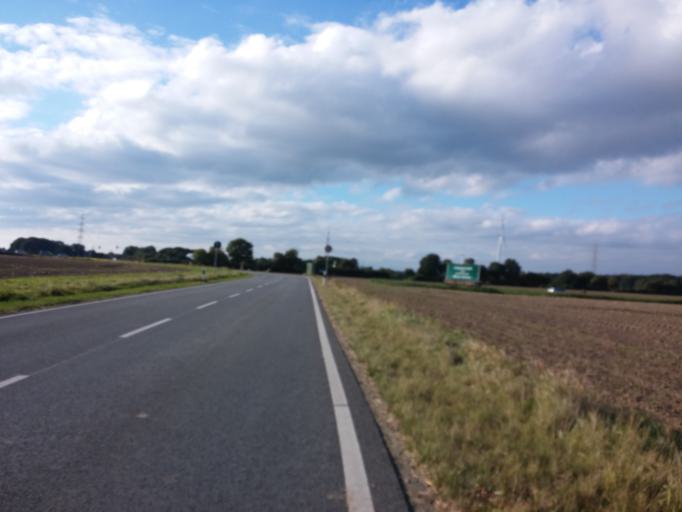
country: DE
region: North Rhine-Westphalia
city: Dorsten
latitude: 51.6205
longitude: 6.9582
